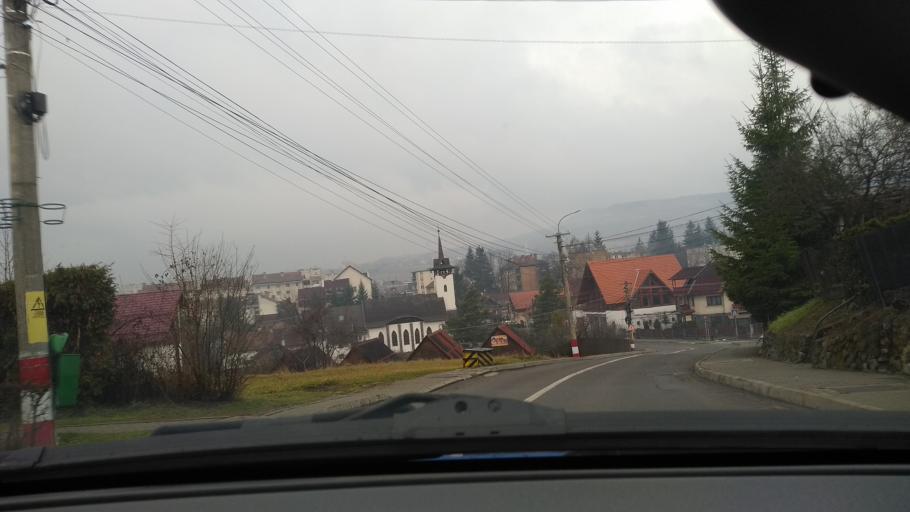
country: RO
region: Mures
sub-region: Oras Sovata
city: Sovata
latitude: 46.5982
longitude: 25.0746
